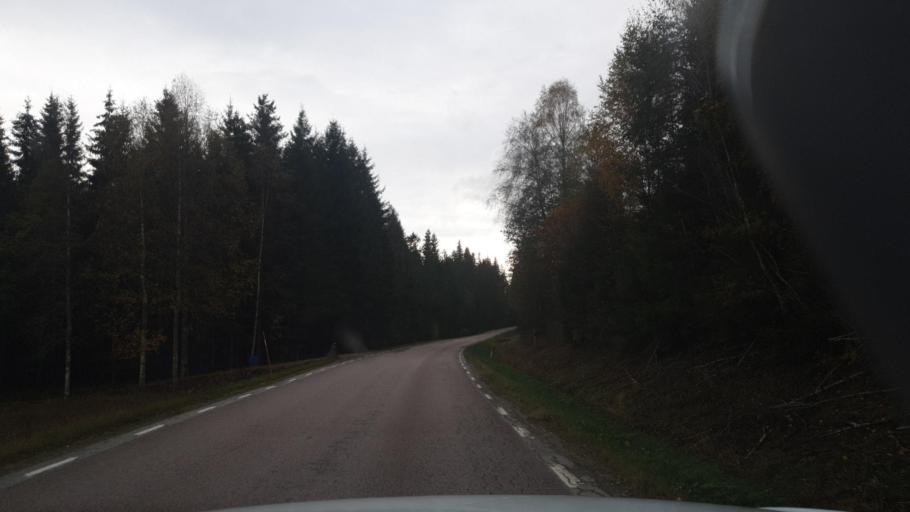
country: SE
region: Vaermland
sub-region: Arvika Kommun
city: Arvika
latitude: 59.7207
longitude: 12.7980
